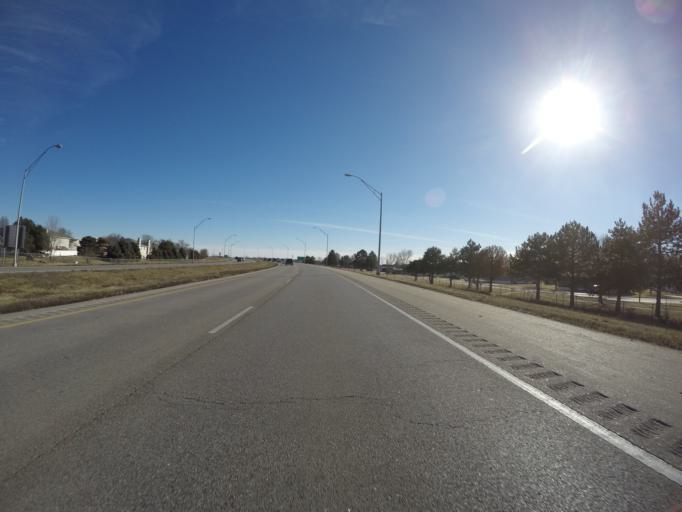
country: US
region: Nebraska
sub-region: Lancaster County
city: Lincoln
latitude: 40.7941
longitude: -96.7381
